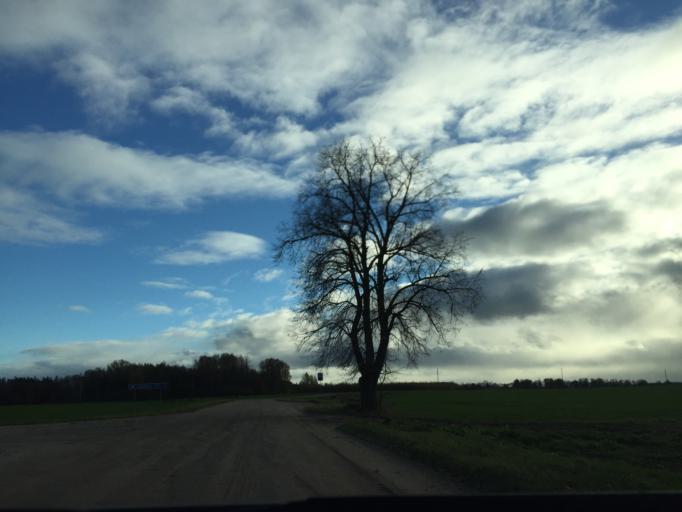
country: LV
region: Tukuma Rajons
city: Tukums
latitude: 56.9351
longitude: 22.9533
